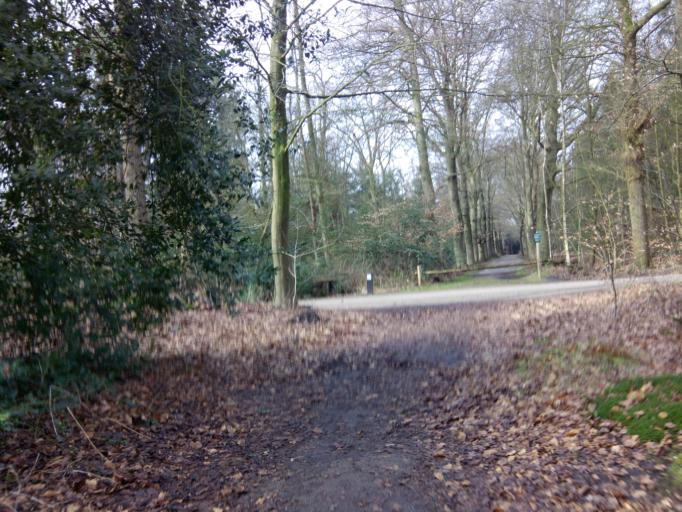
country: NL
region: Utrecht
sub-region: Gemeente Utrechtse Heuvelrug
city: Maarn
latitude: 52.0848
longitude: 5.3854
